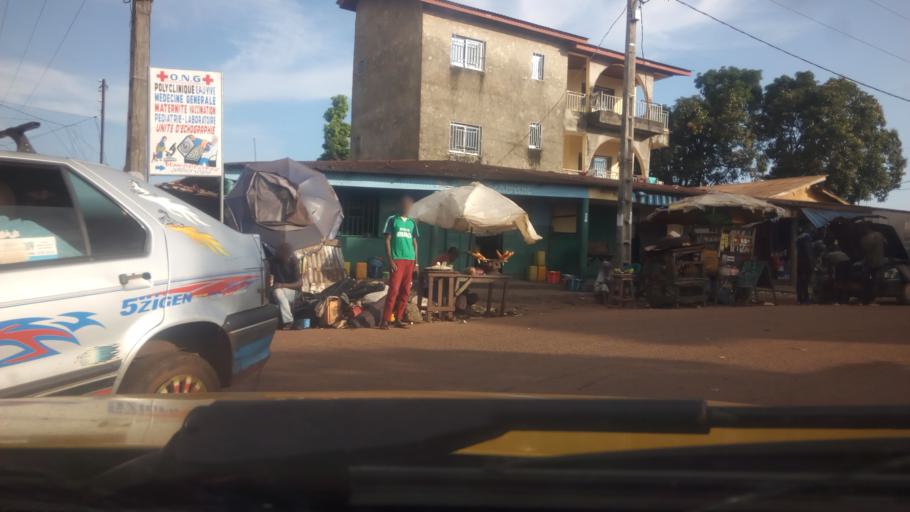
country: GN
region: Conakry
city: Conakry
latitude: 9.6199
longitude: -13.6078
